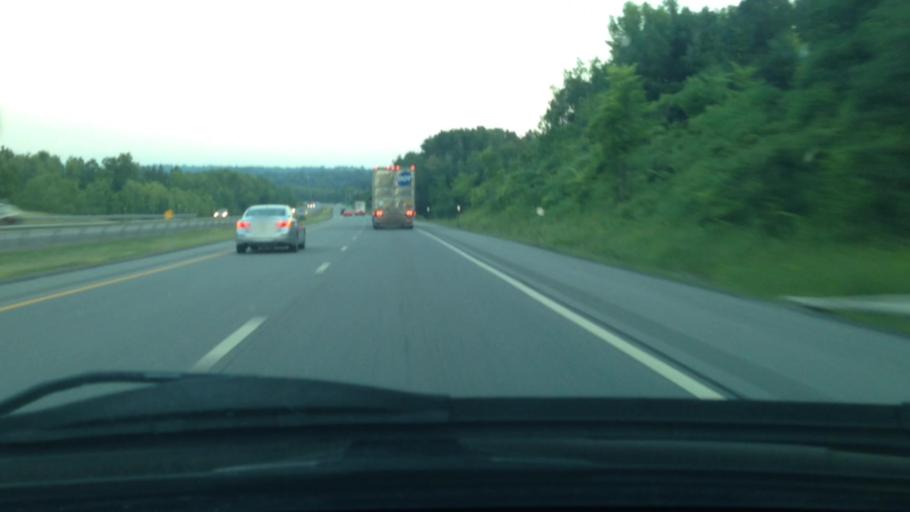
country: US
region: New York
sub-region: Montgomery County
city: Fort Plain
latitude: 42.9513
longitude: -74.6330
